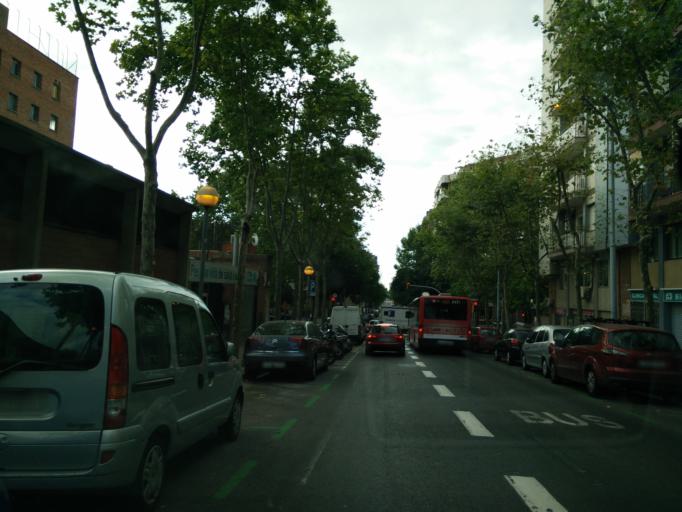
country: ES
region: Catalonia
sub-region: Provincia de Barcelona
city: Sant Marti
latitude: 41.4141
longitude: 2.1930
